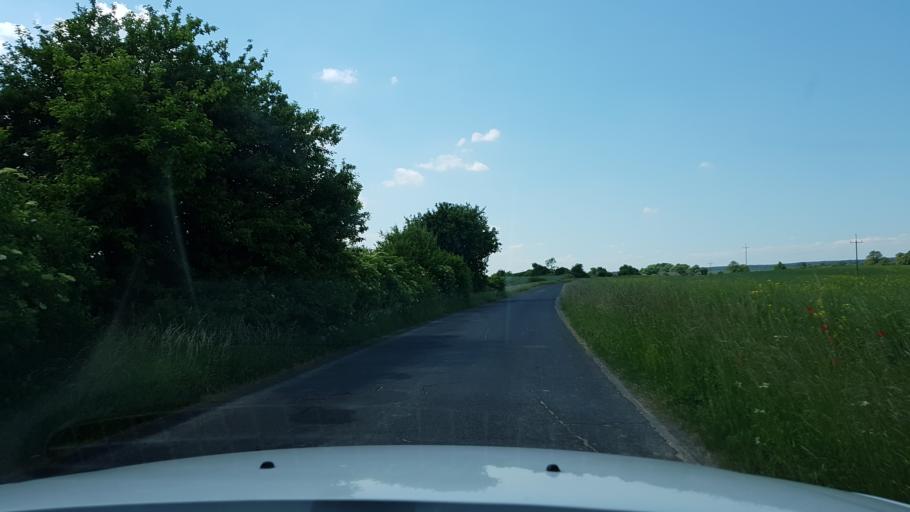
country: PL
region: West Pomeranian Voivodeship
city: Trzcinsko Zdroj
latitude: 52.9942
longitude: 14.5809
